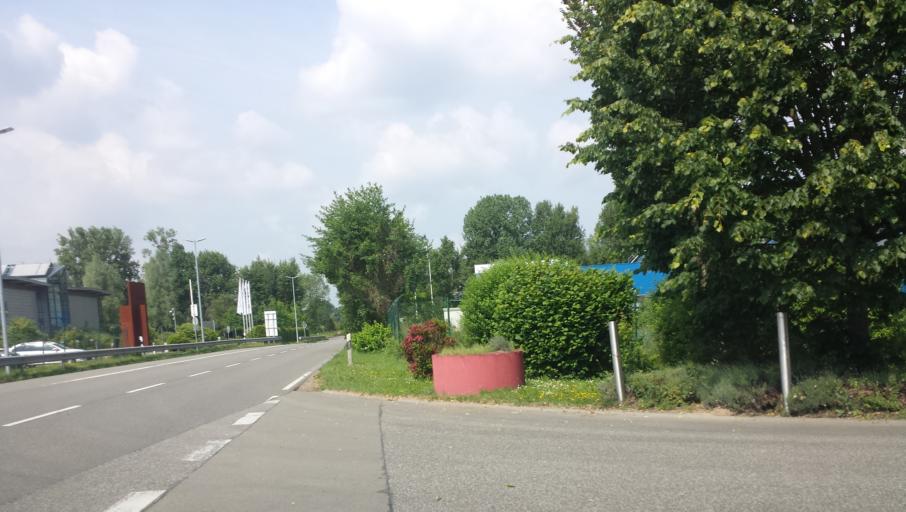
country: DE
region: Rheinland-Pfalz
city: Germersheim
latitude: 49.2045
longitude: 8.3767
